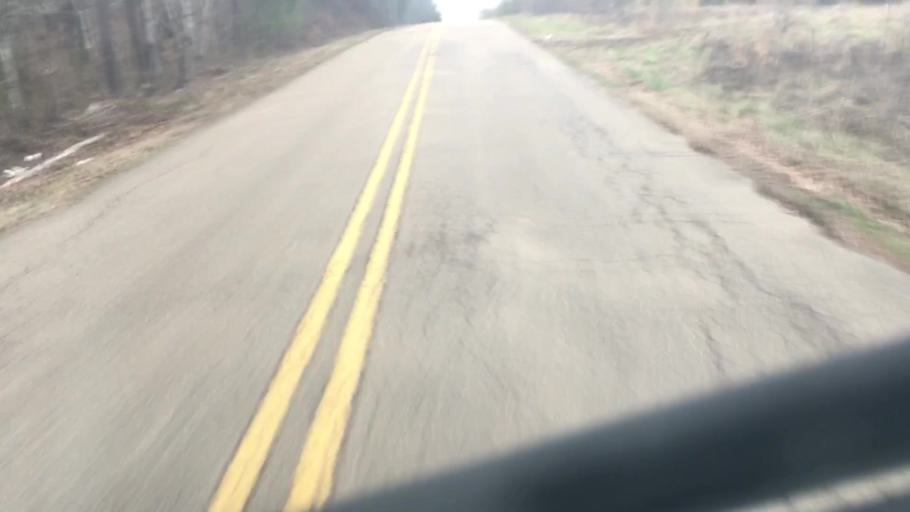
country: US
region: Alabama
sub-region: Walker County
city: Jasper
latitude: 33.8268
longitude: -87.2252
